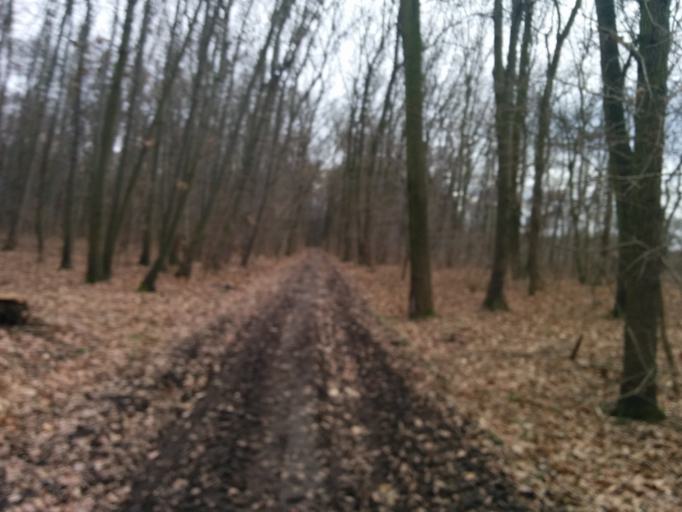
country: CZ
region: Central Bohemia
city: Libis
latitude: 50.2812
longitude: 14.5067
